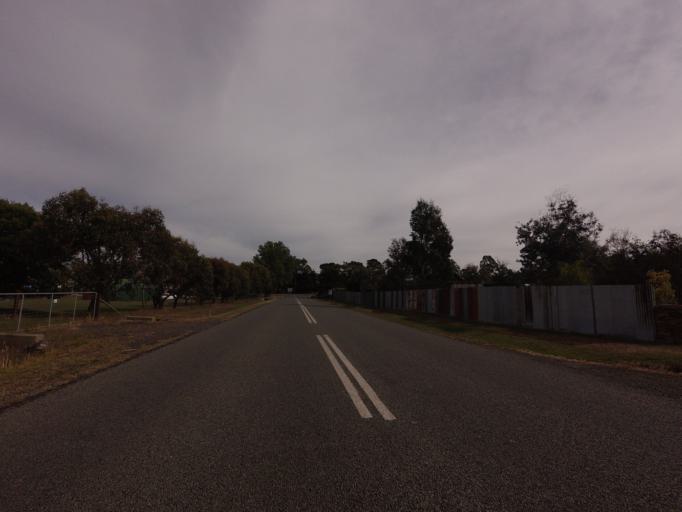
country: AU
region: Tasmania
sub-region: Brighton
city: Bridgewater
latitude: -42.3065
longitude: 147.3636
